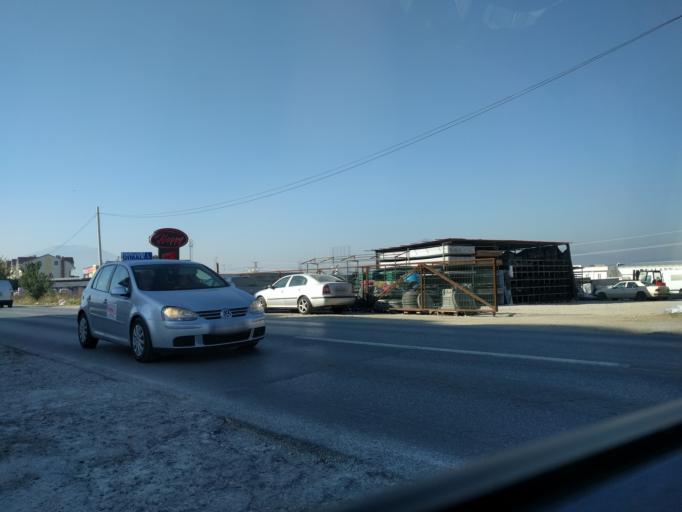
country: XK
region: Prizren
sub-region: Prizren
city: Prizren
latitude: 42.2391
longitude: 20.7624
